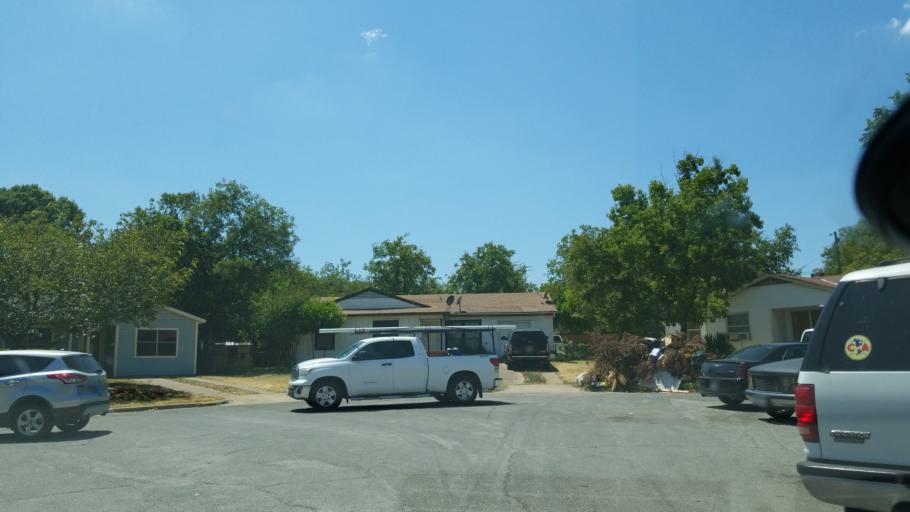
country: US
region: Texas
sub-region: Dallas County
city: Cockrell Hill
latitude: 32.7227
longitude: -96.8851
